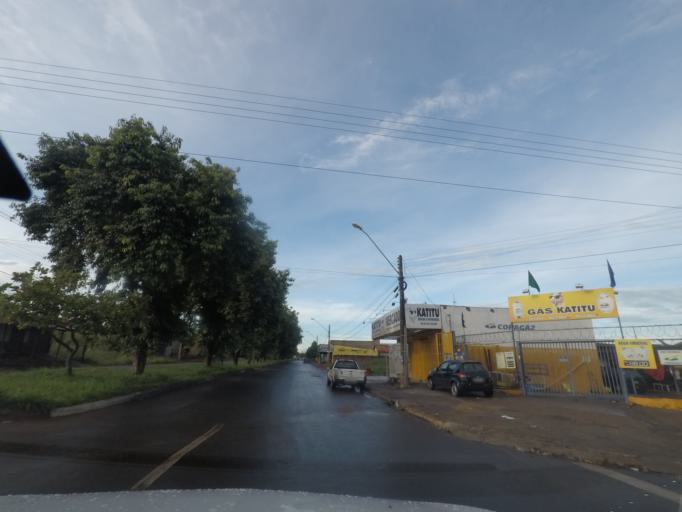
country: BR
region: Goias
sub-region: Goiania
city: Goiania
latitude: -16.7342
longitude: -49.3671
